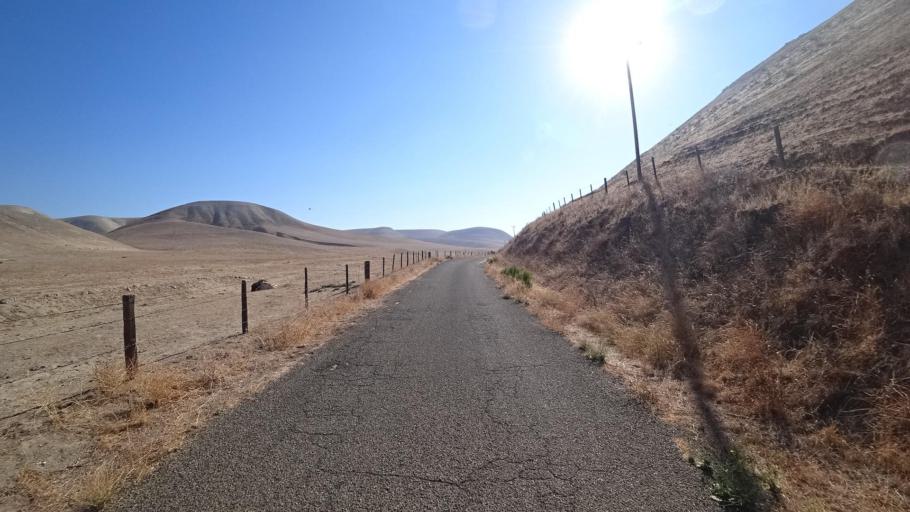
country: US
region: California
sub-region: Monterey County
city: King City
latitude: 36.2000
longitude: -121.0092
